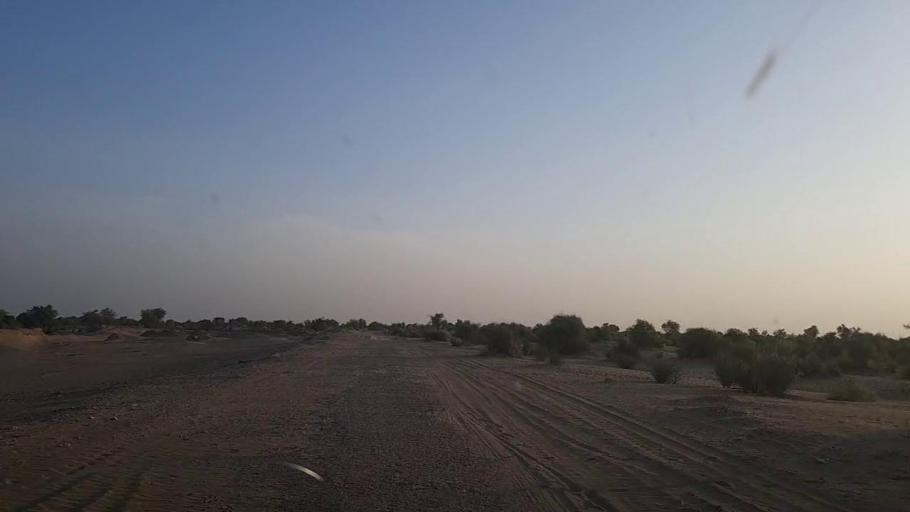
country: PK
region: Sindh
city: Khanpur
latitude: 27.6173
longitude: 69.4418
